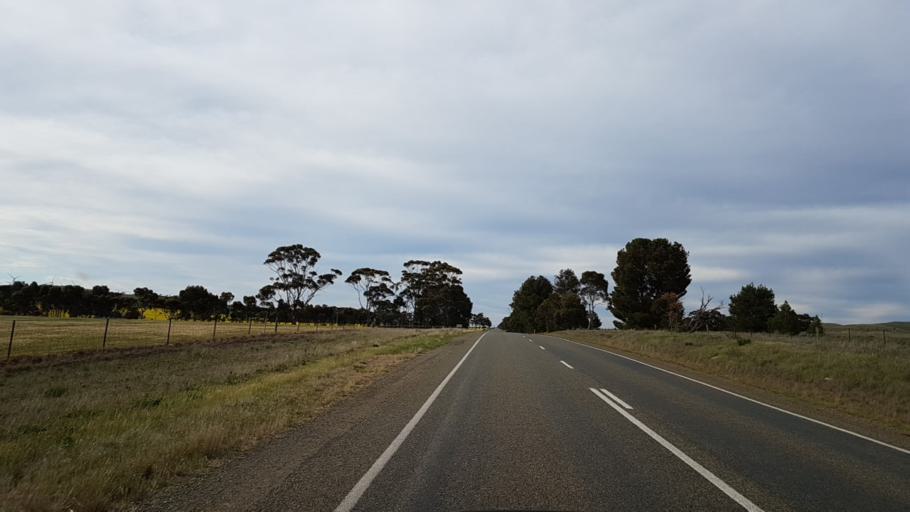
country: AU
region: South Australia
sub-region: Northern Areas
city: Jamestown
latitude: -33.1565
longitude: 138.6144
